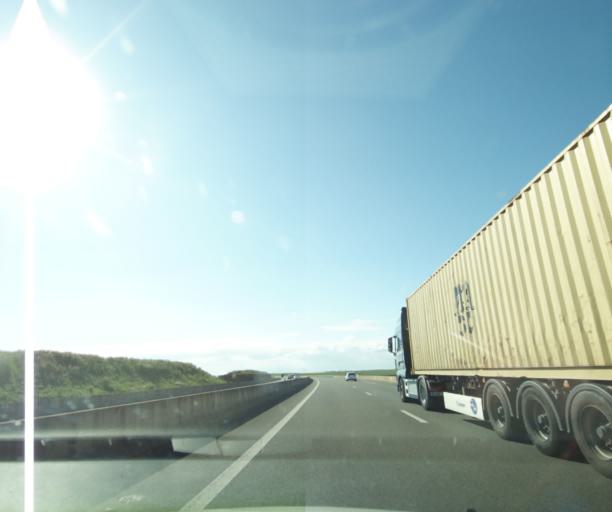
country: FR
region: Centre
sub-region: Departement d'Eure-et-Loir
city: Voves
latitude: 48.2681
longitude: 1.7564
